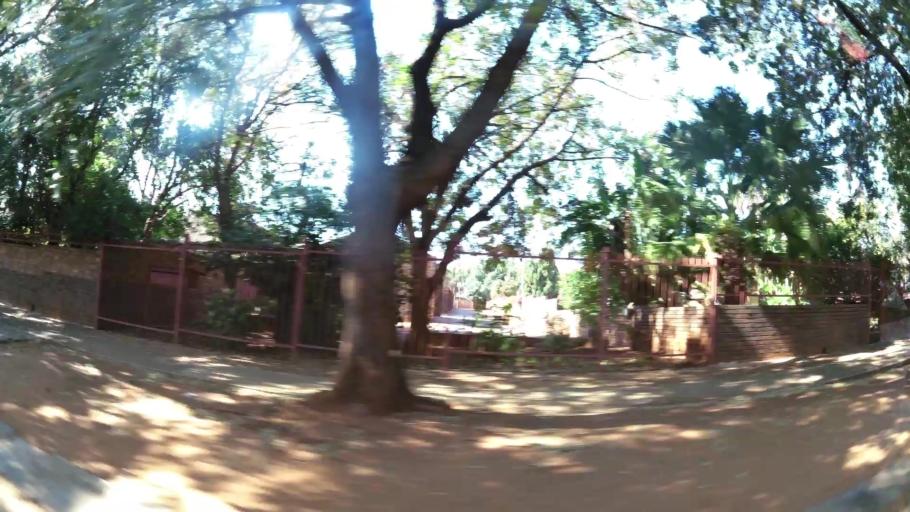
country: ZA
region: Gauteng
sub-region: City of Tshwane Metropolitan Municipality
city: Pretoria
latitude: -25.6815
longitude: 28.2005
